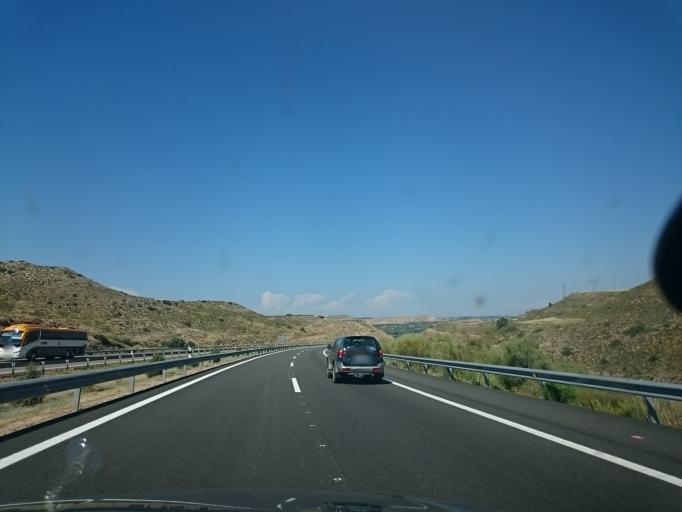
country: ES
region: Aragon
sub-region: Provincia de Huesca
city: Fraga
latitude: 41.4804
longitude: 0.3170
